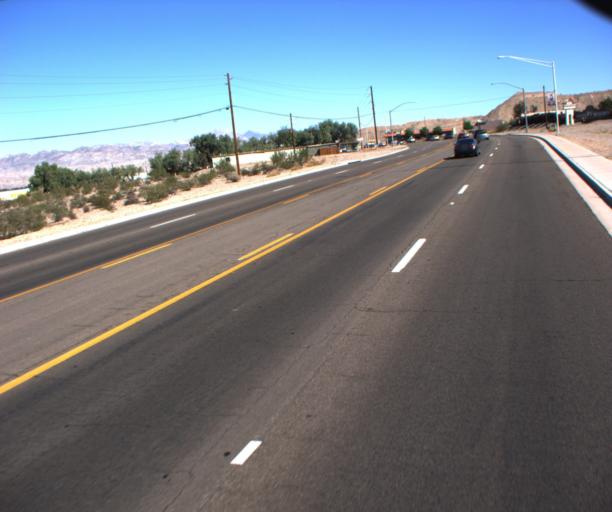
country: US
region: Arizona
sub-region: Mohave County
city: Bullhead City
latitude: 35.0684
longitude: -114.5891
